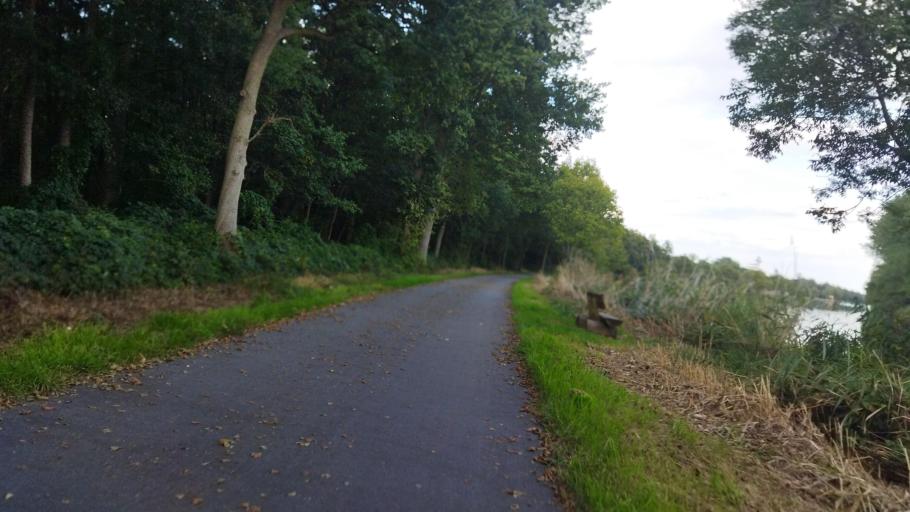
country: DE
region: Lower Saxony
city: Dersum
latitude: 52.9546
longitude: 7.2929
